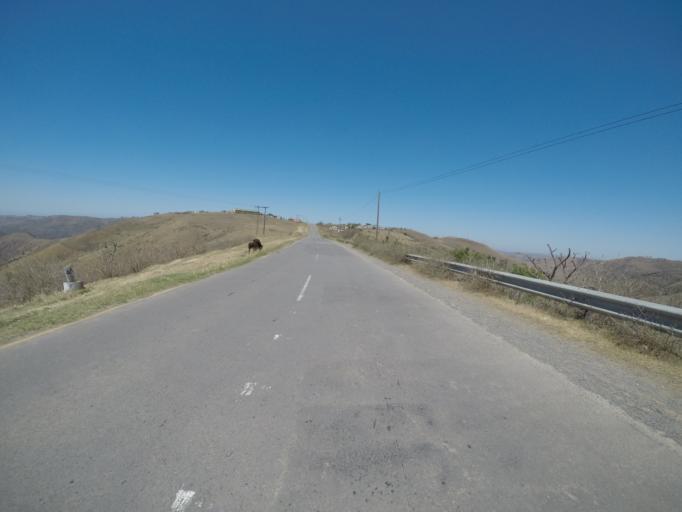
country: ZA
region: Eastern Cape
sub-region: OR Tambo District Municipality
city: Mthatha
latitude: -31.9024
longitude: 28.9463
